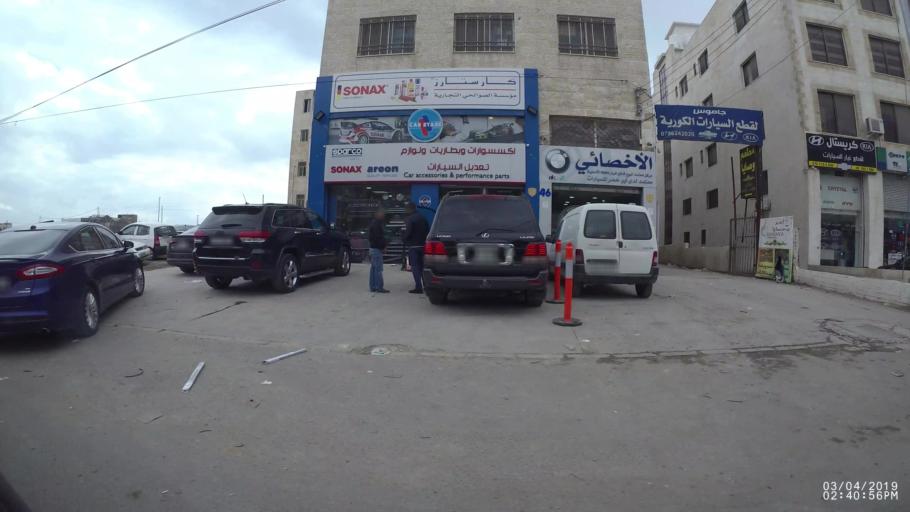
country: JO
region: Amman
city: Wadi as Sir
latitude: 31.9413
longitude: 35.8407
